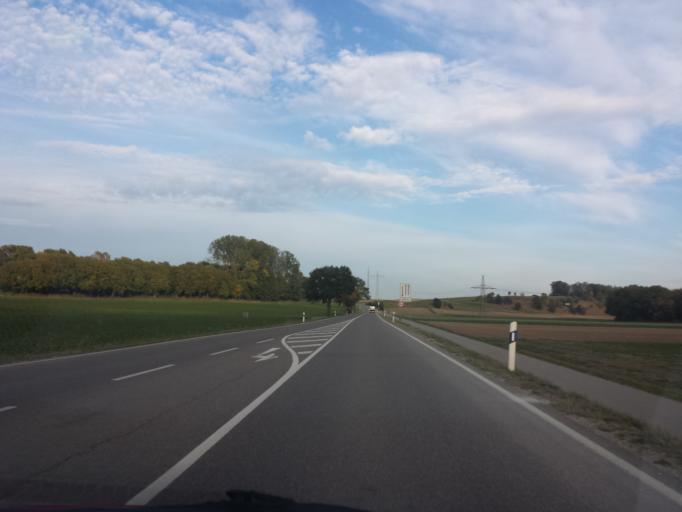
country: DE
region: Bavaria
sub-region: Upper Bavaria
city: Buxheim
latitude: 48.7683
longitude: 11.2905
